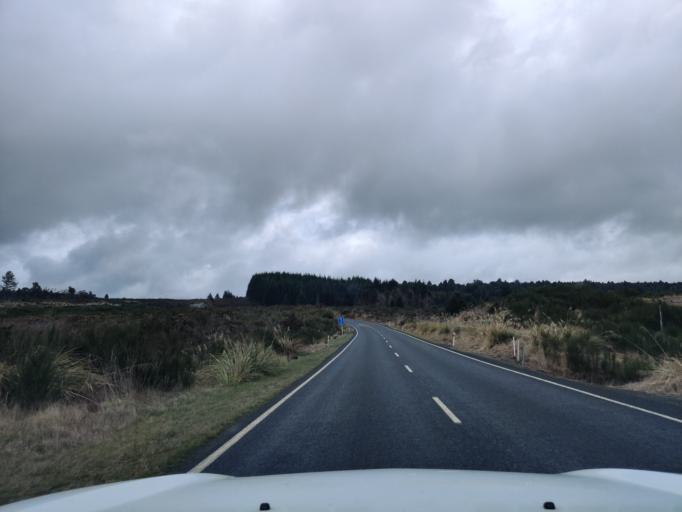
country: NZ
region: Manawatu-Wanganui
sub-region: Ruapehu District
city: Waiouru
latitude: -39.2060
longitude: 175.4026
